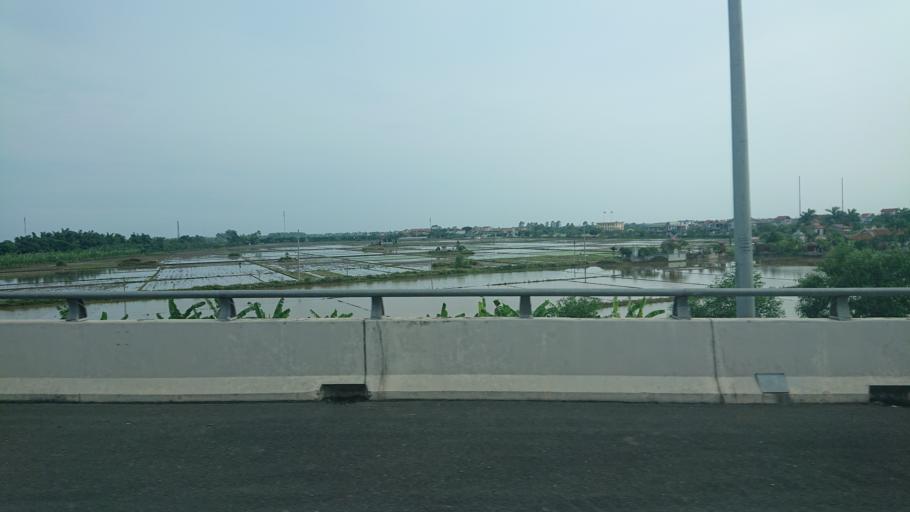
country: VN
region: Hai Duong
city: Tu Ky
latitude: 20.8341
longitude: 106.4385
